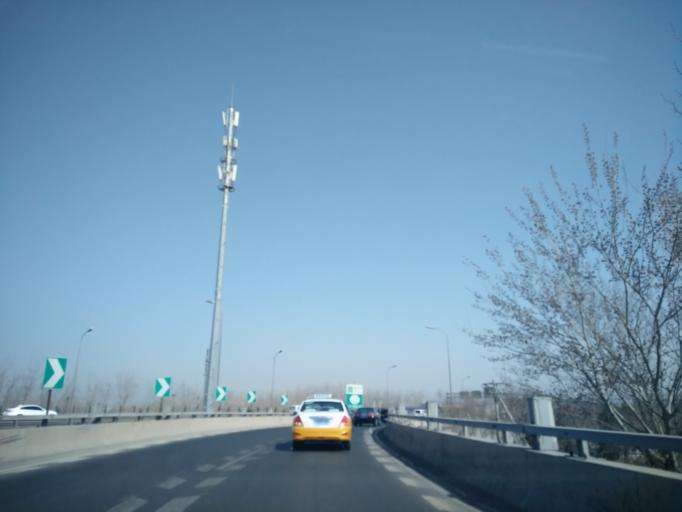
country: CN
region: Beijing
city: Jiugong
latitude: 39.8135
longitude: 116.4872
